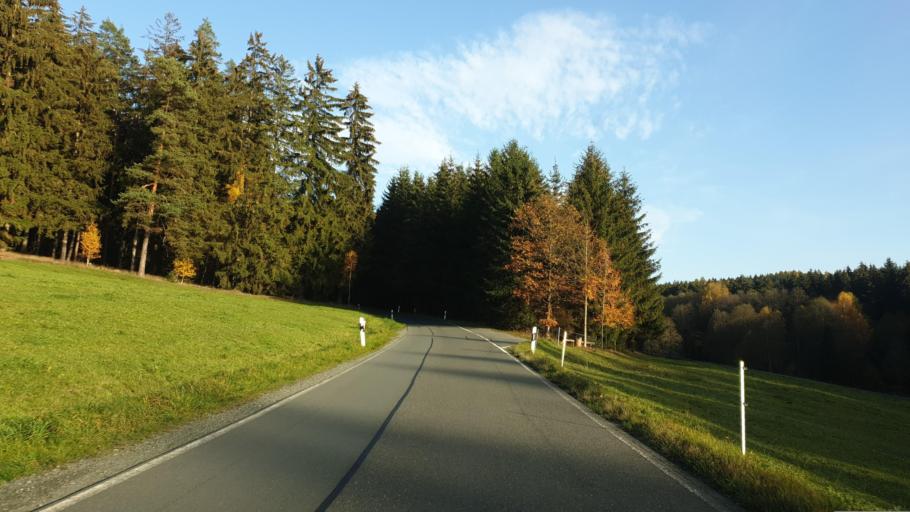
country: DE
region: Saxony
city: Markneukirchen
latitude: 50.2676
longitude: 12.3108
